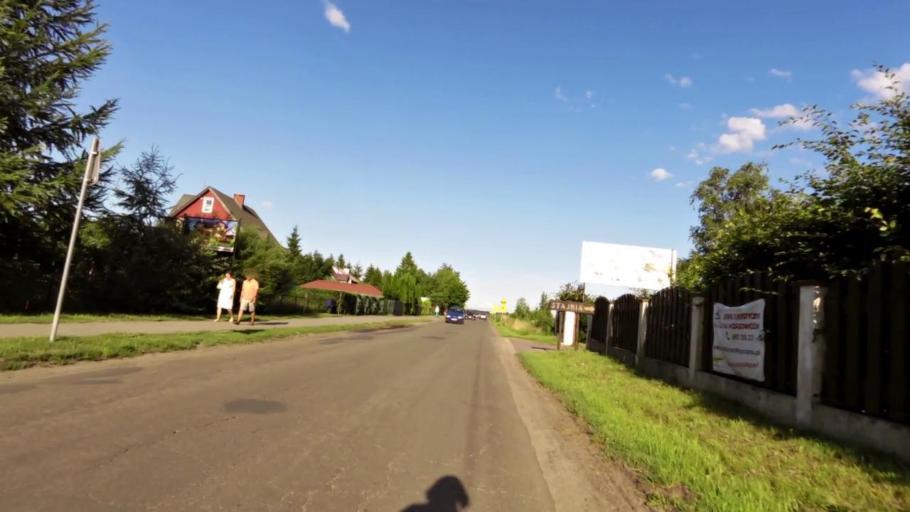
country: PL
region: West Pomeranian Voivodeship
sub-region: Powiat slawienski
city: Darlowo
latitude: 54.3945
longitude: 16.3498
